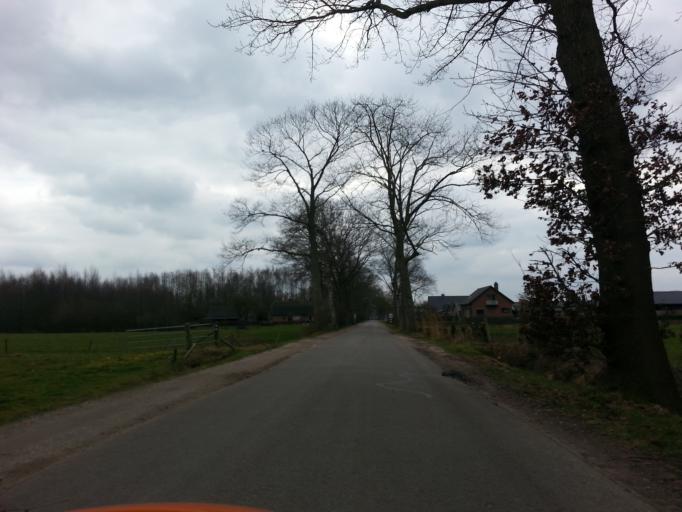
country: NL
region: Gelderland
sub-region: Gemeente Barneveld
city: Terschuur
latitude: 52.1120
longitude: 5.5002
